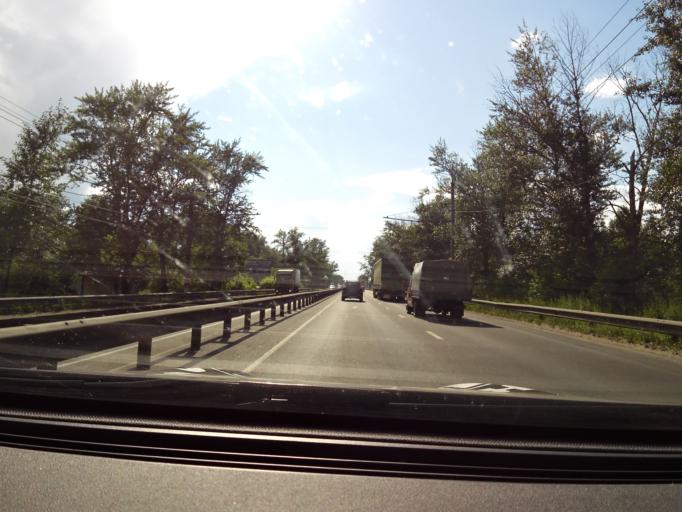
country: RU
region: Nizjnij Novgorod
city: Gorbatovka
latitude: 56.3112
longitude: 43.8074
